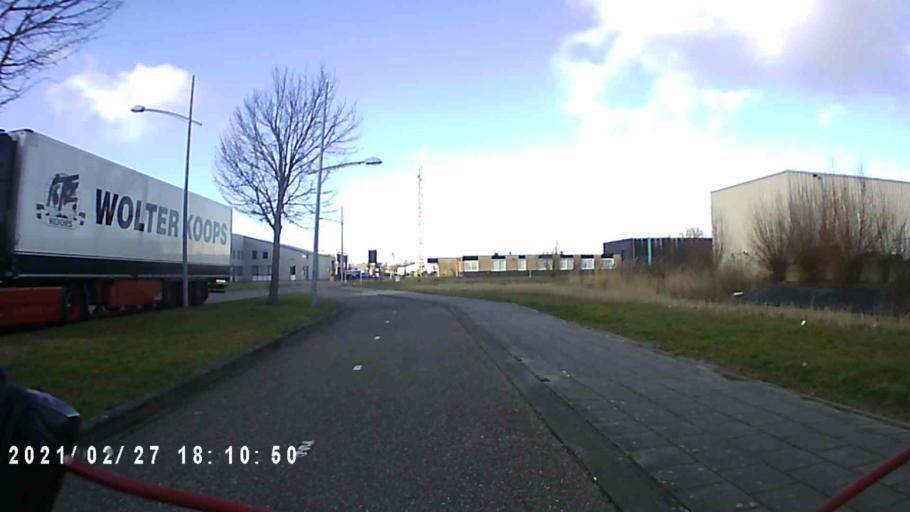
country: NL
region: Groningen
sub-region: Gemeente Bedum
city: Bedum
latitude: 53.2939
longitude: 6.5957
